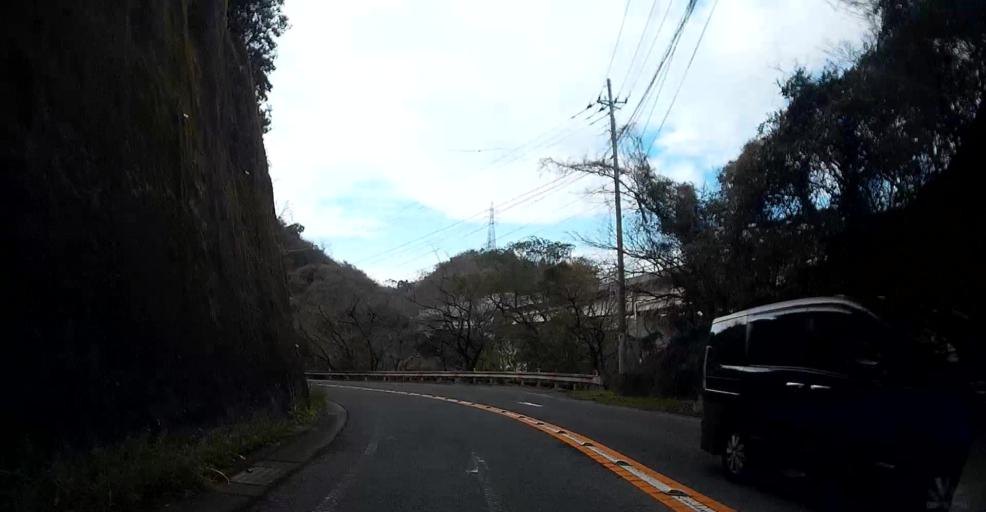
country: JP
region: Kumamoto
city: Yatsushiro
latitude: 32.6138
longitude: 130.4554
